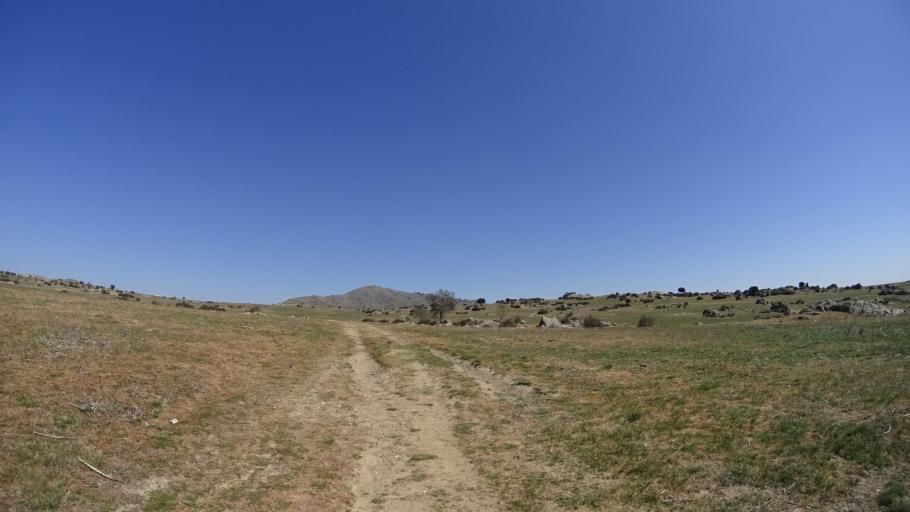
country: ES
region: Madrid
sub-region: Provincia de Madrid
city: Colmenar Viejo
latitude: 40.7052
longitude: -3.7551
